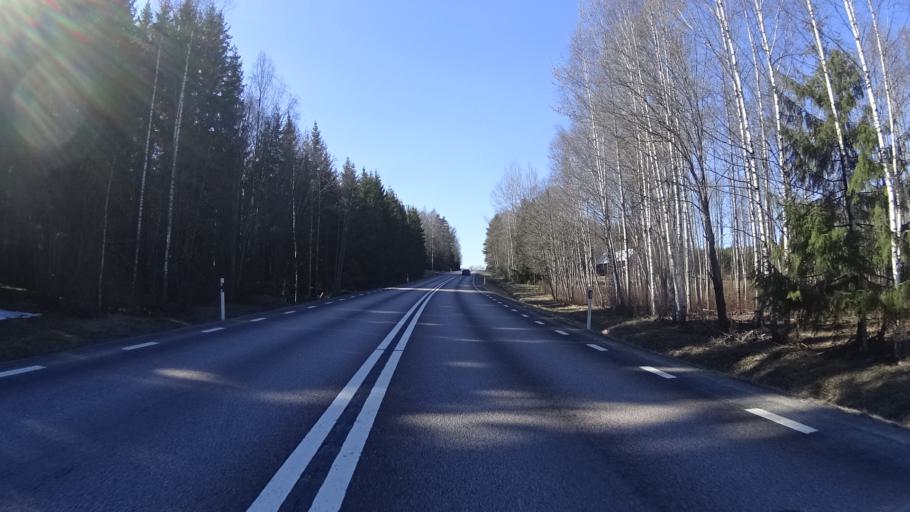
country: SE
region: Vaermland
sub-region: Karlstads Kommun
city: Edsvalla
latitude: 59.5242
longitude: 13.1422
